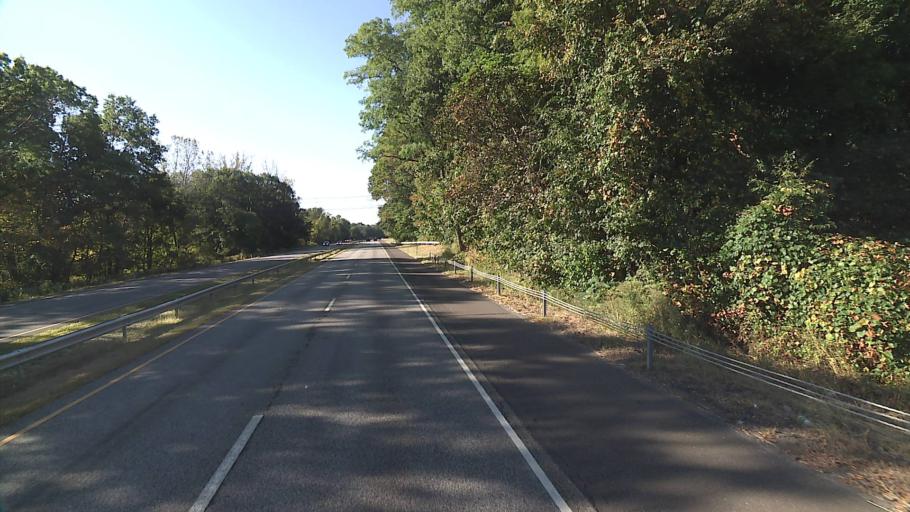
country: US
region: Connecticut
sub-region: New Haven County
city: Wallingford
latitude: 41.4513
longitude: -72.8412
